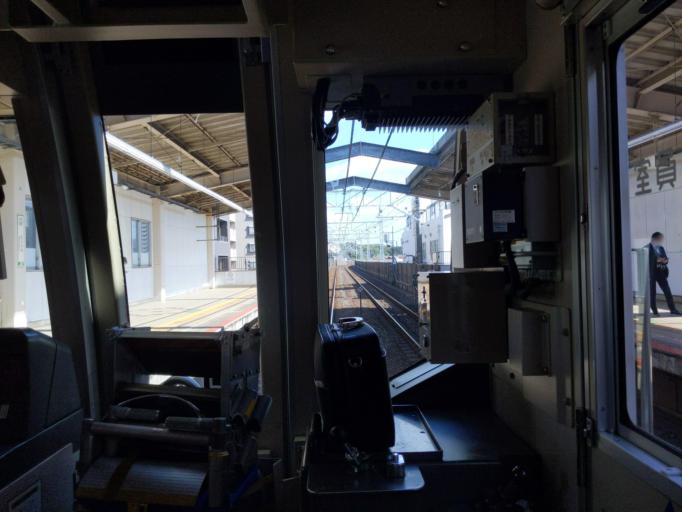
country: JP
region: Chiba
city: Yotsukaido
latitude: 35.7234
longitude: 140.1195
